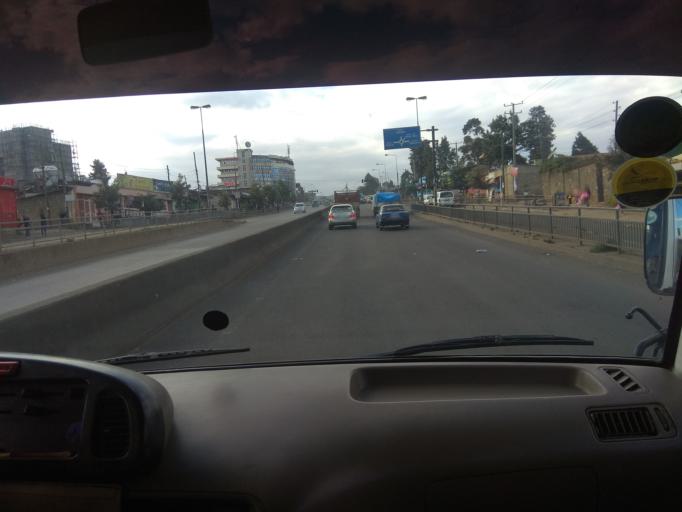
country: ET
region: Adis Abeba
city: Addis Ababa
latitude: 9.0318
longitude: 38.7147
